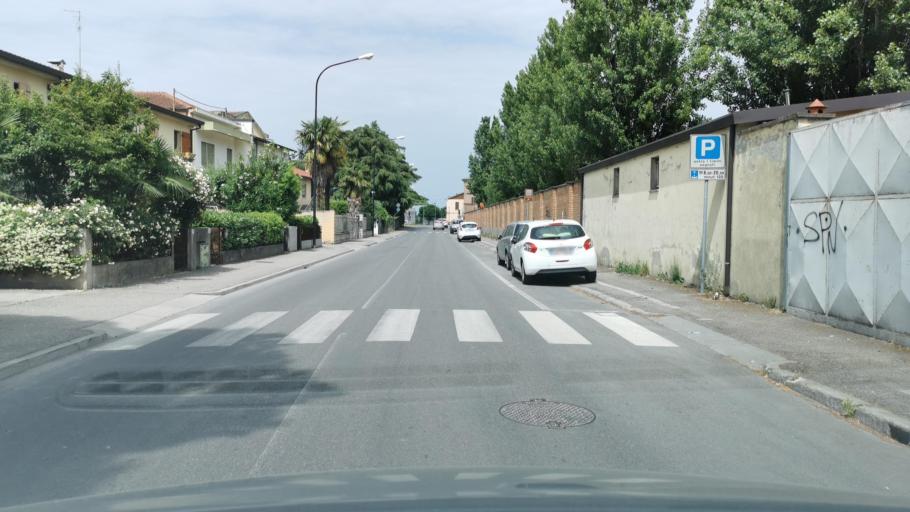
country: IT
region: Emilia-Romagna
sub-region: Provincia di Ravenna
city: Bagnacavallo
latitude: 44.4177
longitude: 11.9731
